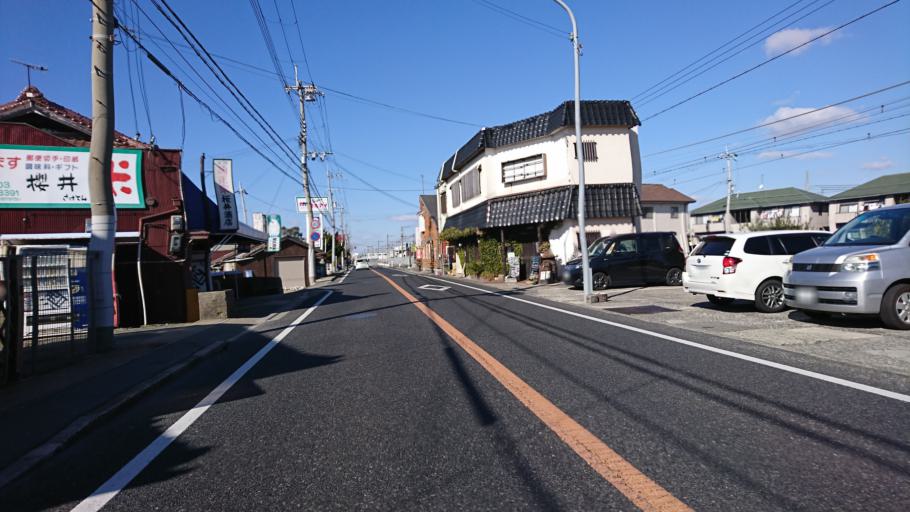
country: JP
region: Hyogo
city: Akashi
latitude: 34.6711
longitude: 134.9355
